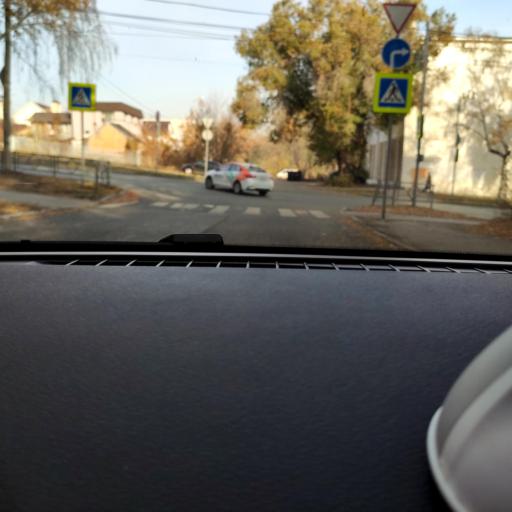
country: RU
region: Samara
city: Samara
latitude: 53.1971
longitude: 50.2103
